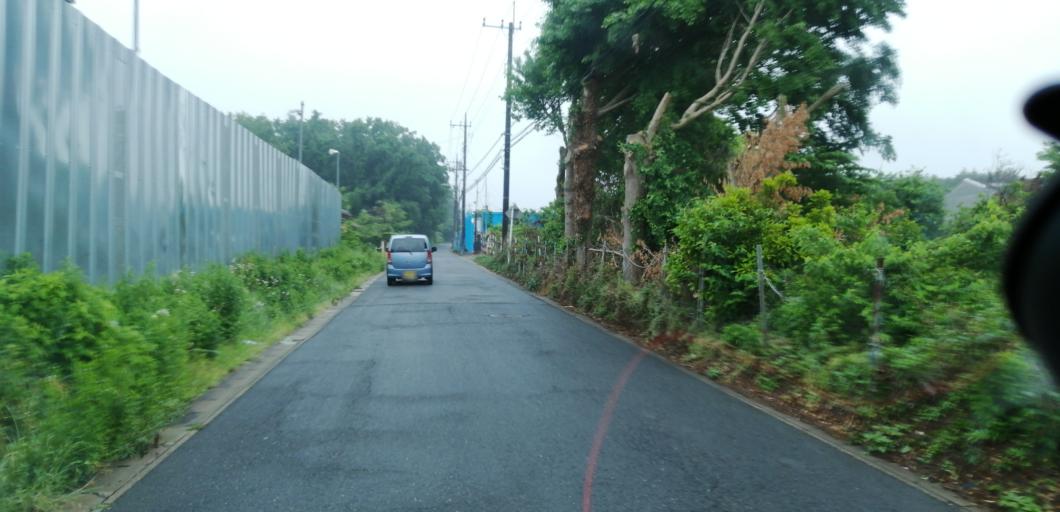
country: JP
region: Chiba
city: Ichihara
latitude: 35.4894
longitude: 140.1486
